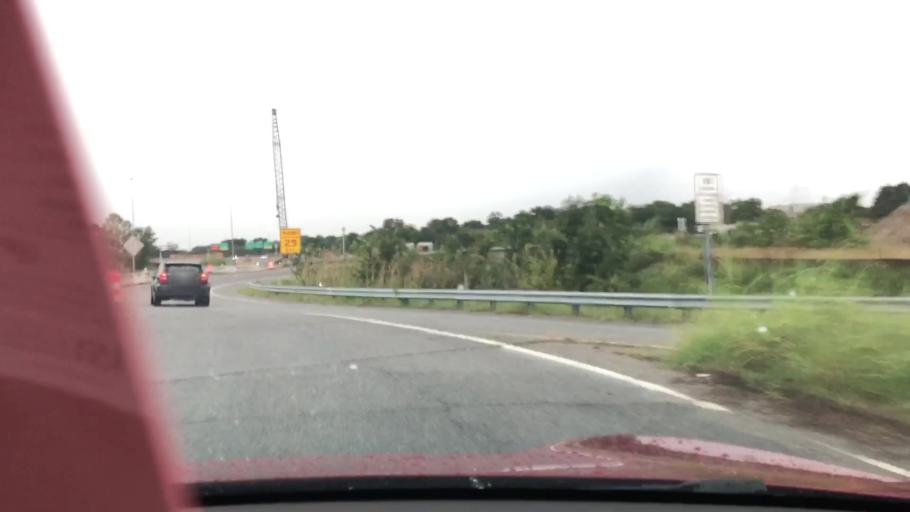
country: US
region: Virginia
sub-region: City of Chesapeake
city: Chesapeake
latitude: 36.8443
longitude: -76.1849
